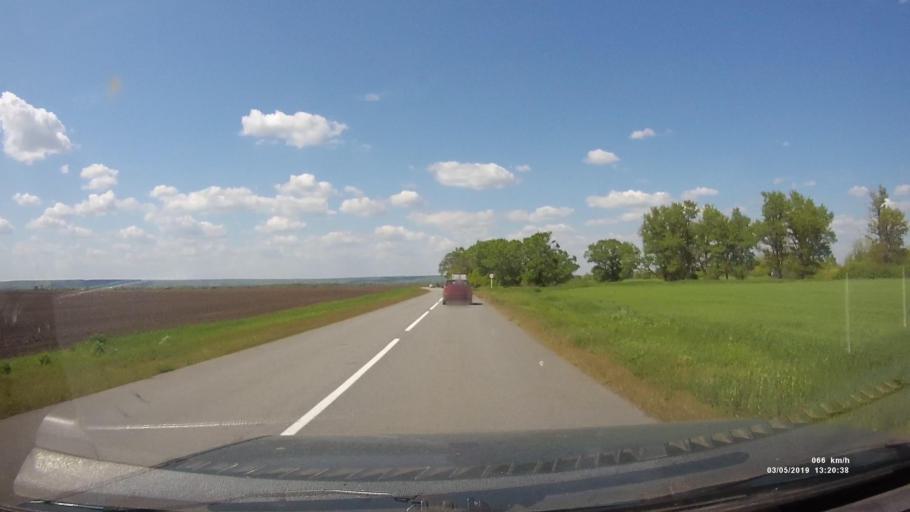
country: RU
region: Rostov
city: Semikarakorsk
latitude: 47.5479
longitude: 40.7522
